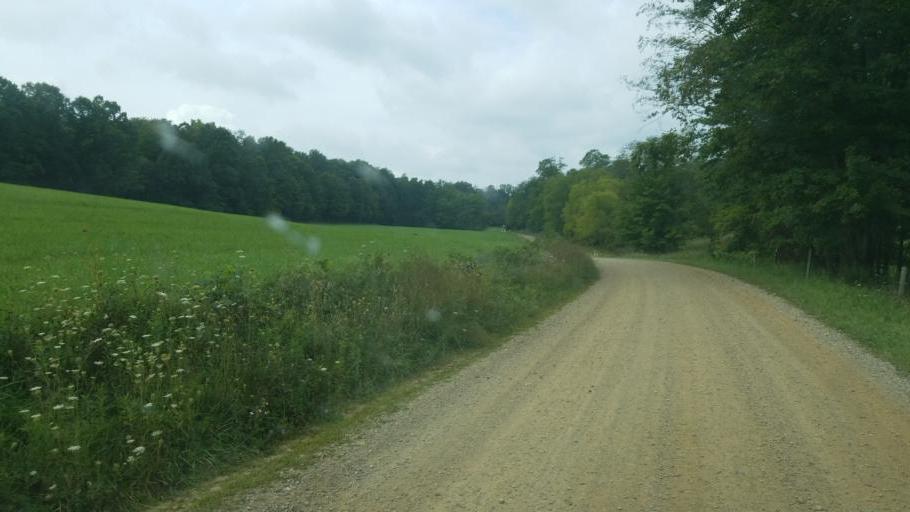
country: US
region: Ohio
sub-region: Knox County
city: Danville
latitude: 40.4773
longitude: -82.3177
